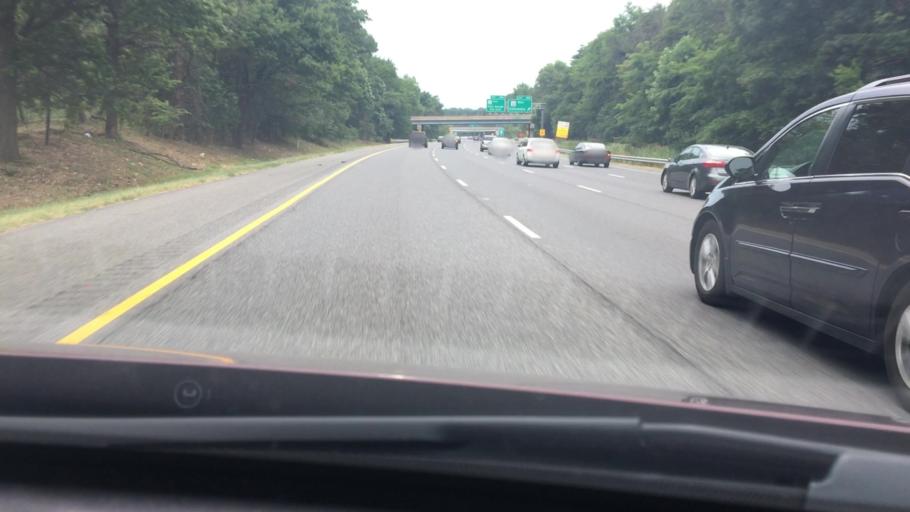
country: US
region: Maryland
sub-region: Howard County
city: Savage
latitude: 39.1607
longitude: -76.8208
